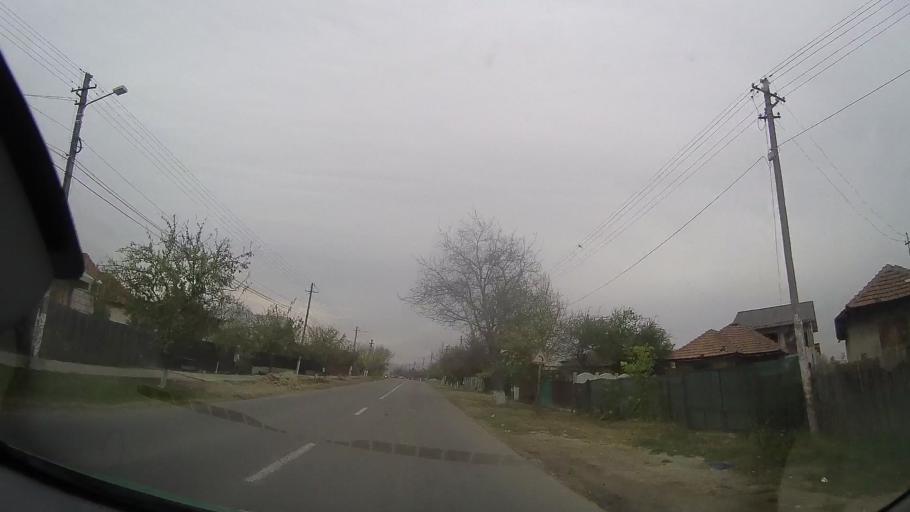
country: RO
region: Prahova
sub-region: Comuna Albesti-Paleologu
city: Albesti-Paleologu
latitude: 44.9581
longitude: 26.2316
